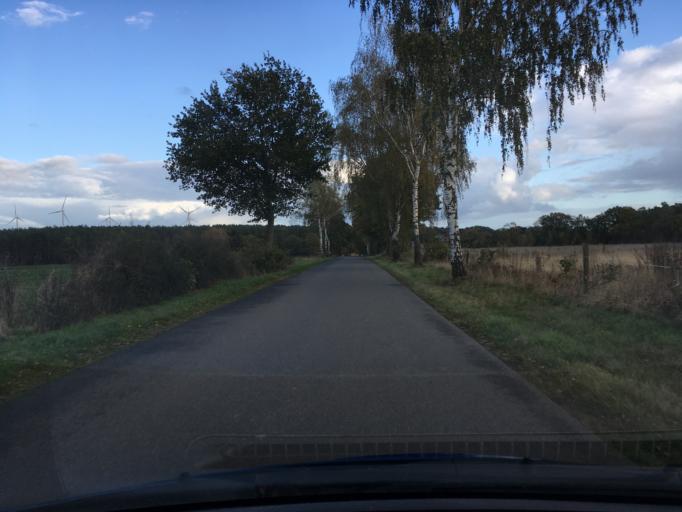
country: DE
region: Lower Saxony
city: Reinstorf
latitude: 53.2504
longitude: 10.5461
